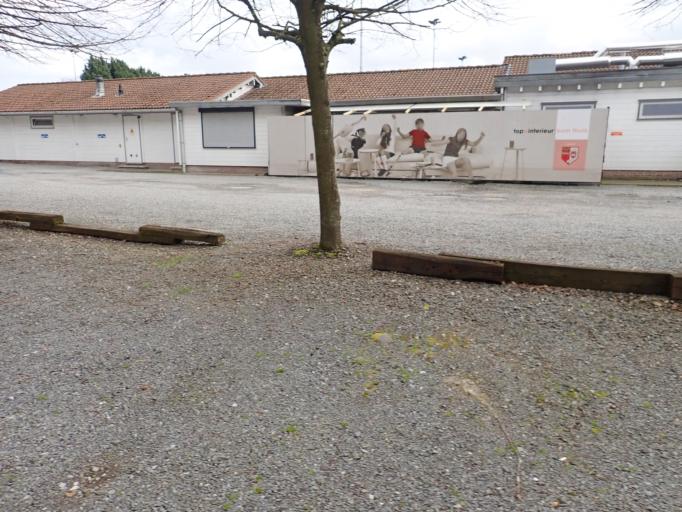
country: BE
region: Flanders
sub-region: Provincie Antwerpen
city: Schilde
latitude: 51.2874
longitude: 4.5719
